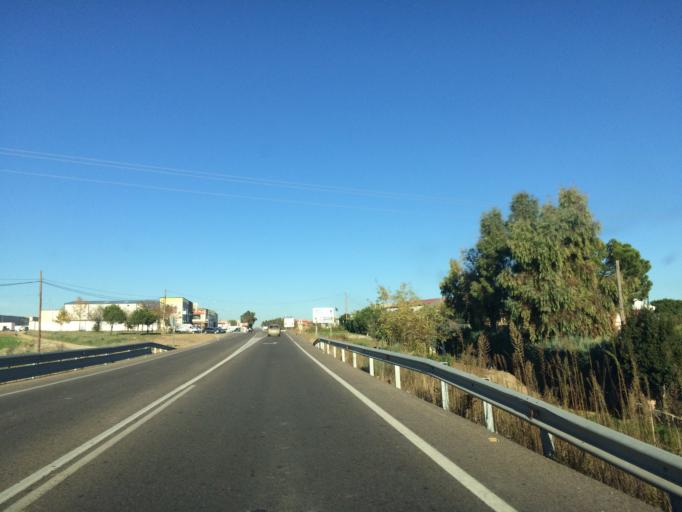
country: ES
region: Castille-La Mancha
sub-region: Province of Toledo
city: Carranque
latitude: 40.1793
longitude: -3.8888
